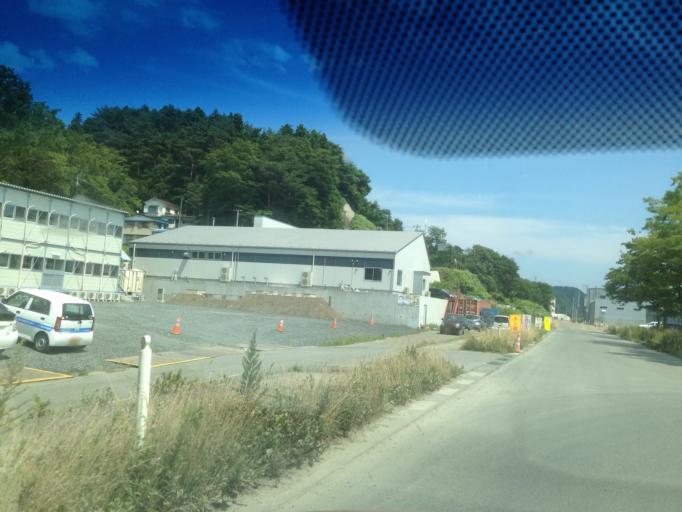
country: JP
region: Iwate
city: Otsuchi
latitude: 39.3552
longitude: 141.9224
